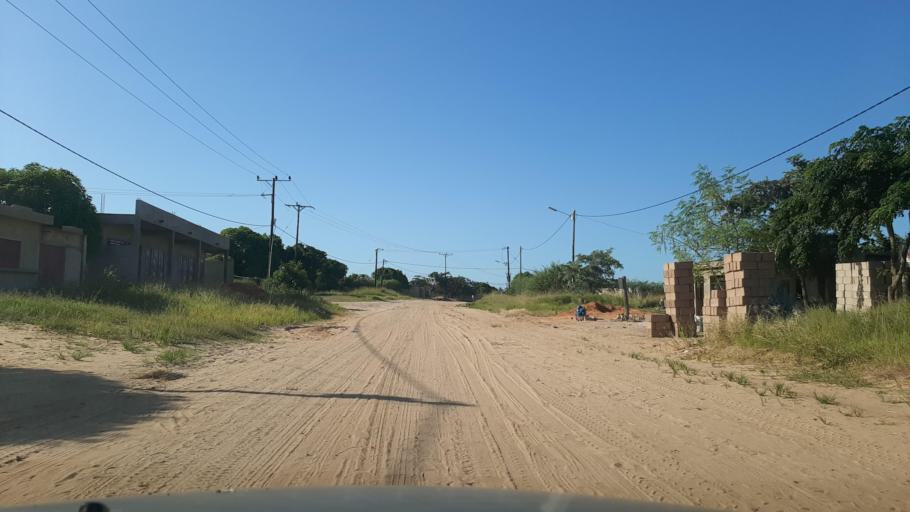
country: MZ
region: Maputo City
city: Maputo
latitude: -25.7650
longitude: 32.5473
